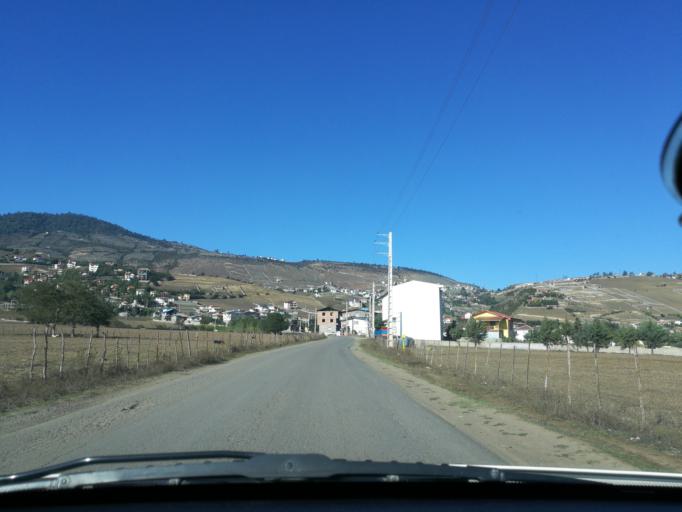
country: IR
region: Mazandaran
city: `Abbasabad
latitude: 36.5439
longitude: 51.1834
